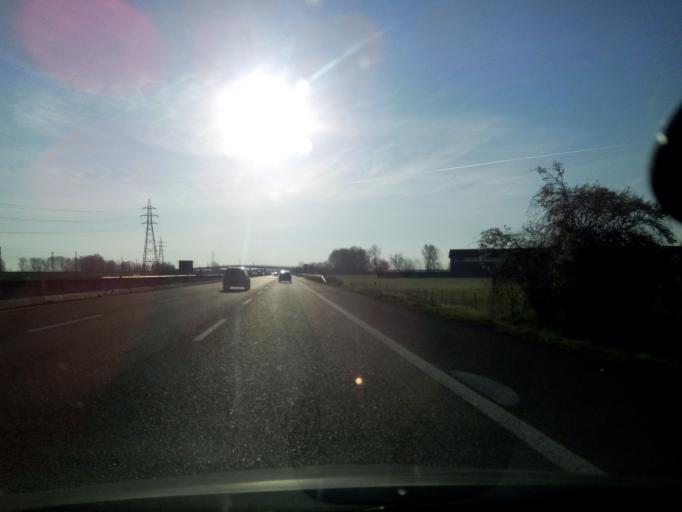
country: IT
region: Emilia-Romagna
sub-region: Provincia di Parma
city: Soragna
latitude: 44.8869
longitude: 10.1047
